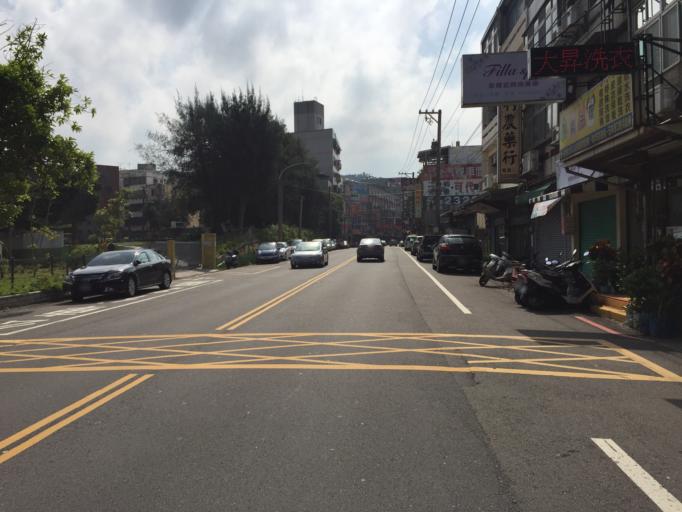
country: TW
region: Taiwan
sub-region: Hsinchu
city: Hsinchu
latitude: 24.7899
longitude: 120.9656
